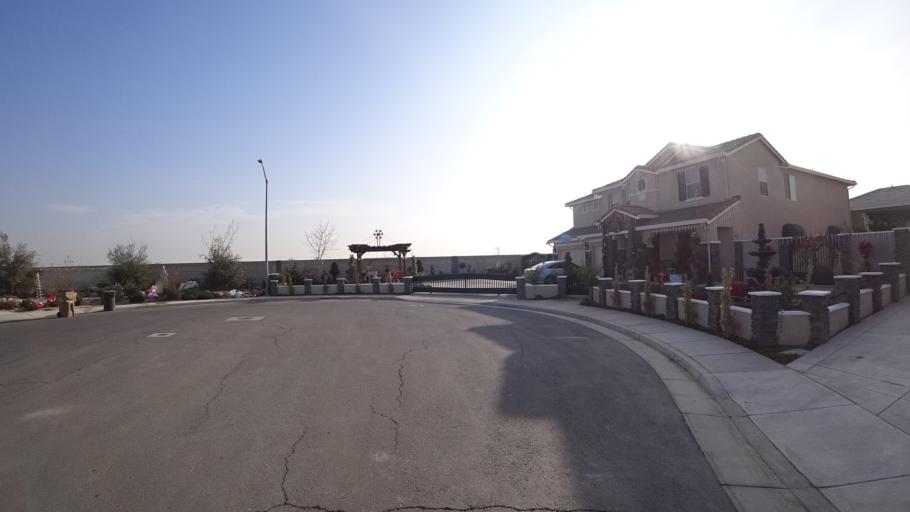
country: US
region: California
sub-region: Kern County
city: Greenacres
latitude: 35.4319
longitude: -119.1016
